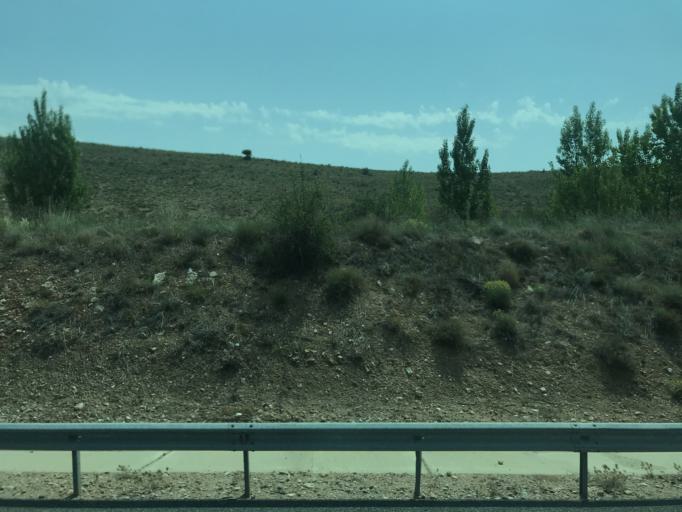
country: ES
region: Castille and Leon
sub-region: Provincia de Segovia
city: Honrubia de la Cuesta
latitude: 41.5164
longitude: -3.7168
